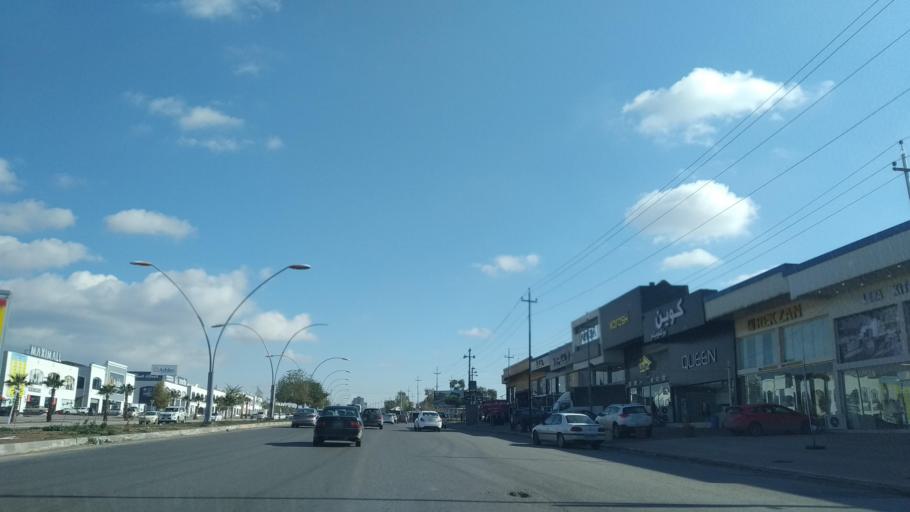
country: IQ
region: Arbil
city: Erbil
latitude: 36.2005
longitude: 44.0956
